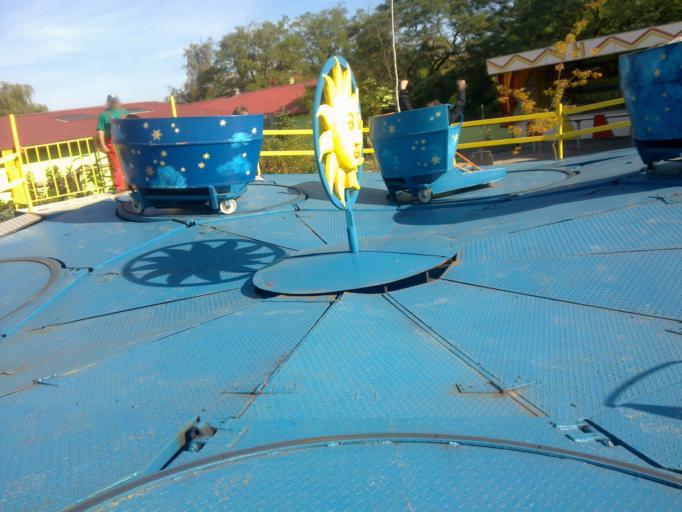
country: PL
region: Lubusz
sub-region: Powiat sulecinski
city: Krzeszyce
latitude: 52.6613
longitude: 14.9942
